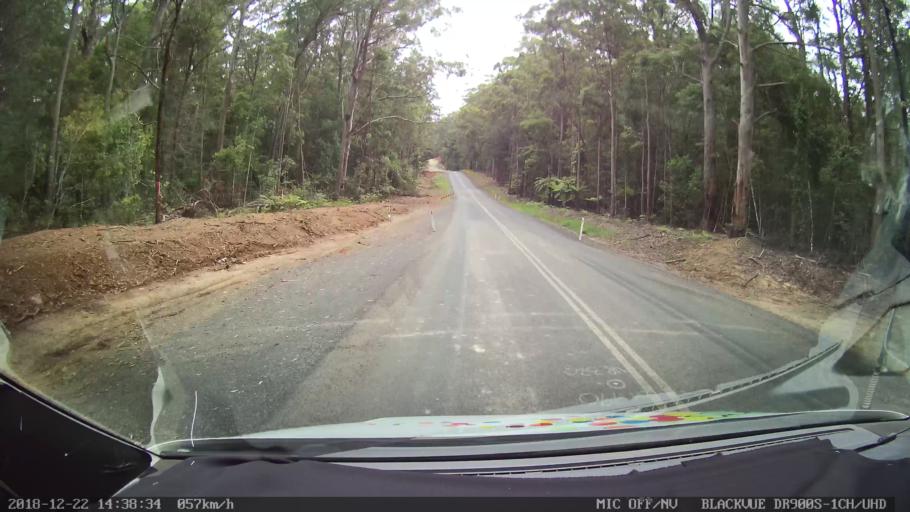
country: AU
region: New South Wales
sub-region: Bellingen
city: Dorrigo
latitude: -30.1392
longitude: 152.5968
